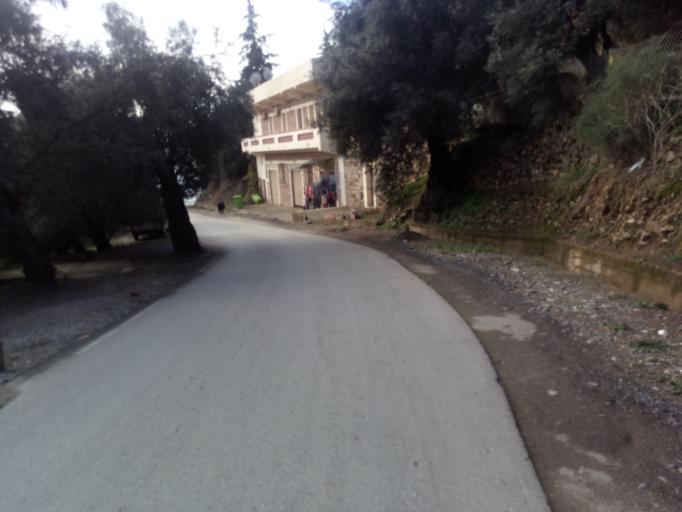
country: DZ
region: Tizi Ouzou
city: Chemini
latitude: 36.6088
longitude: 4.6485
